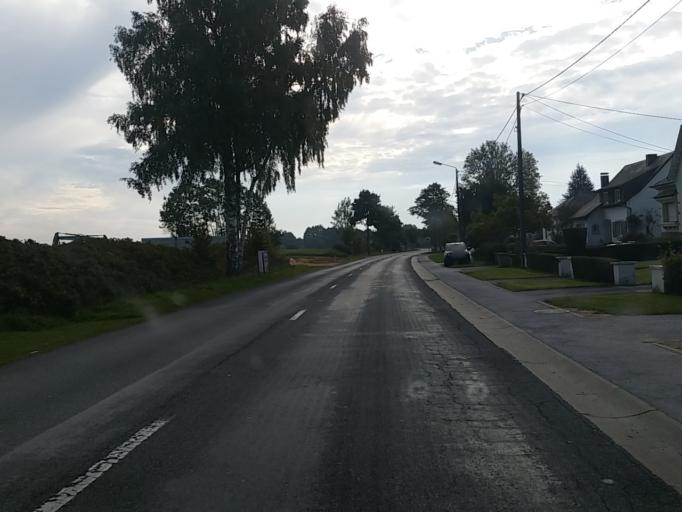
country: BE
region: Wallonia
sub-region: Province du Luxembourg
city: Florenville
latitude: 49.6961
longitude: 5.3202
